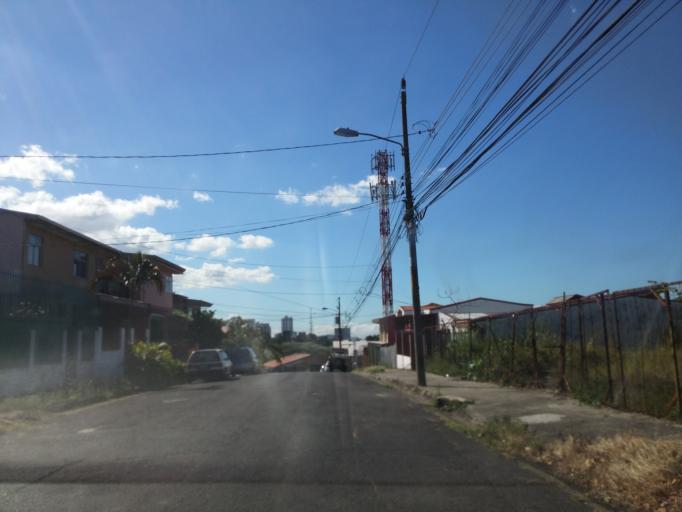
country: CR
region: San Jose
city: Colima
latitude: 9.9432
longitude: -84.0929
